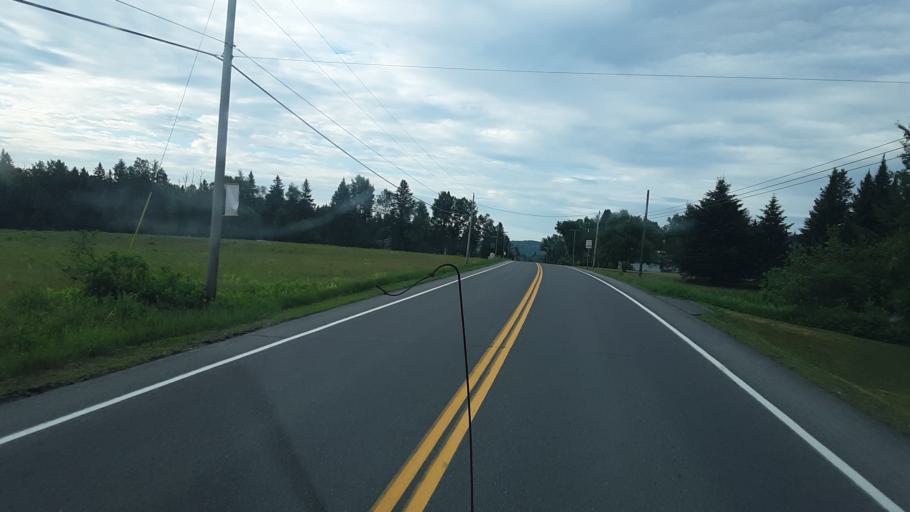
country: US
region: Maine
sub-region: Penobscot County
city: Patten
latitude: 45.9145
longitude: -68.4384
